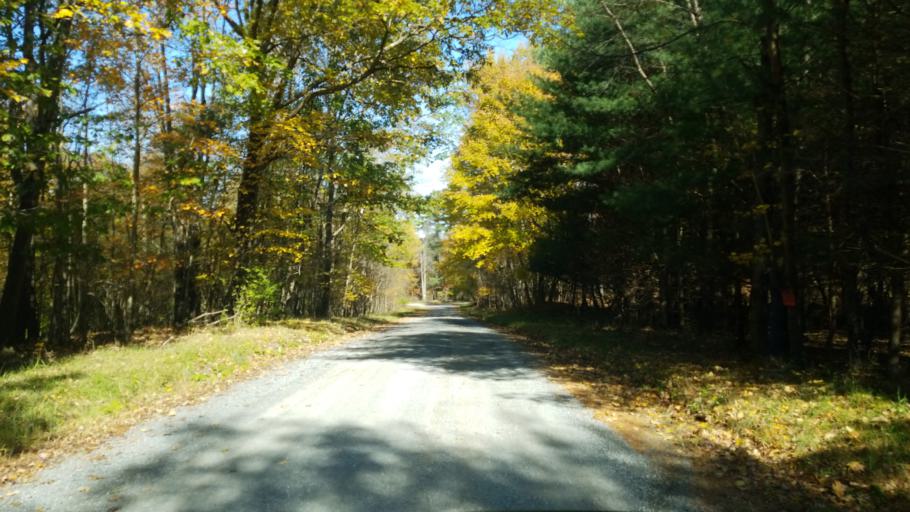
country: US
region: Pennsylvania
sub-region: Jefferson County
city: Falls Creek
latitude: 41.1893
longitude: -78.7816
